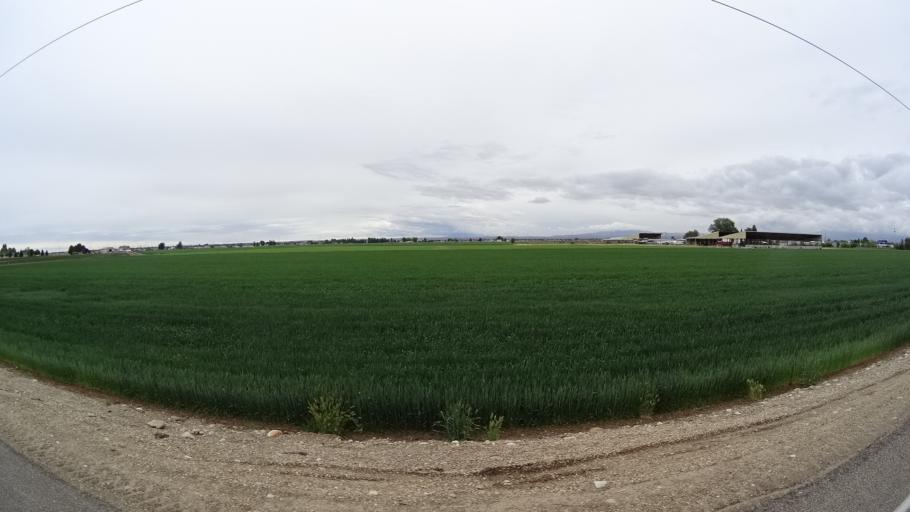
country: US
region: Idaho
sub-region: Ada County
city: Meridian
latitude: 43.6336
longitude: -116.4477
